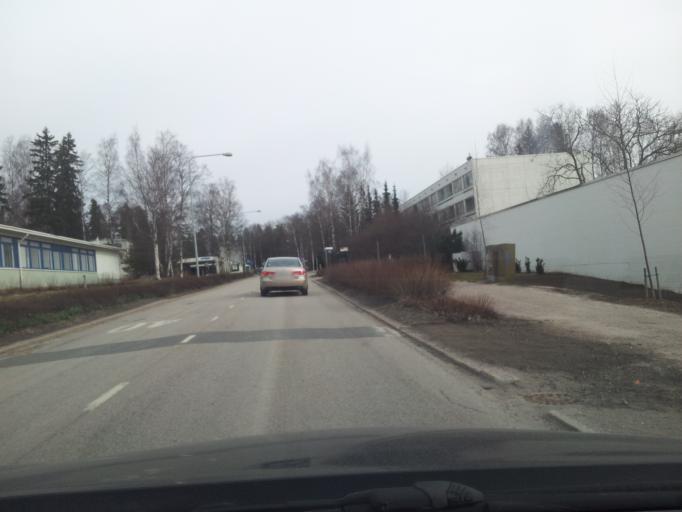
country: FI
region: Uusimaa
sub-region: Helsinki
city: Otaniemi
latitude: 60.1860
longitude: 24.7964
